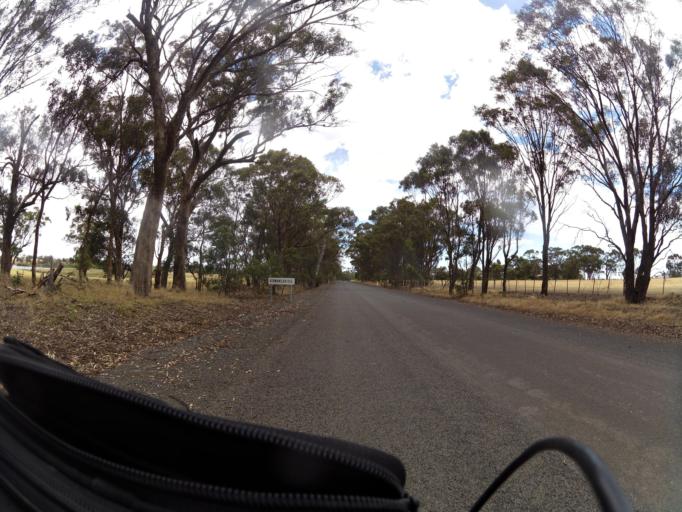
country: AU
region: Victoria
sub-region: Campaspe
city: Kyabram
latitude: -36.7373
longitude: 145.1410
